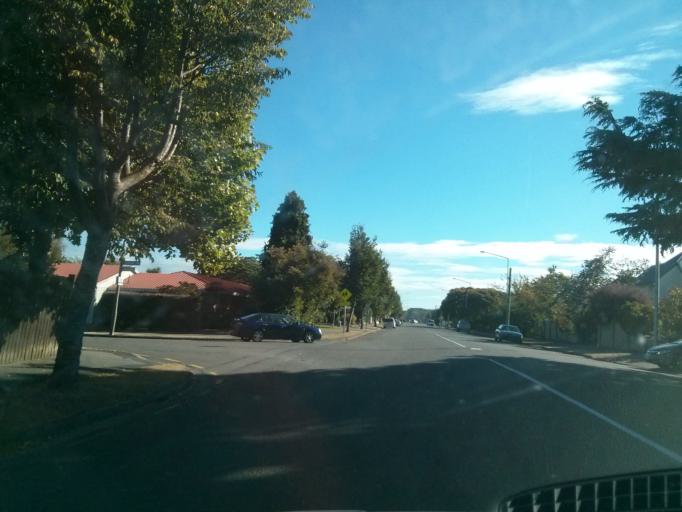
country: NZ
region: Canterbury
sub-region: Christchurch City
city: Christchurch
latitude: -43.4959
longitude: 172.5636
